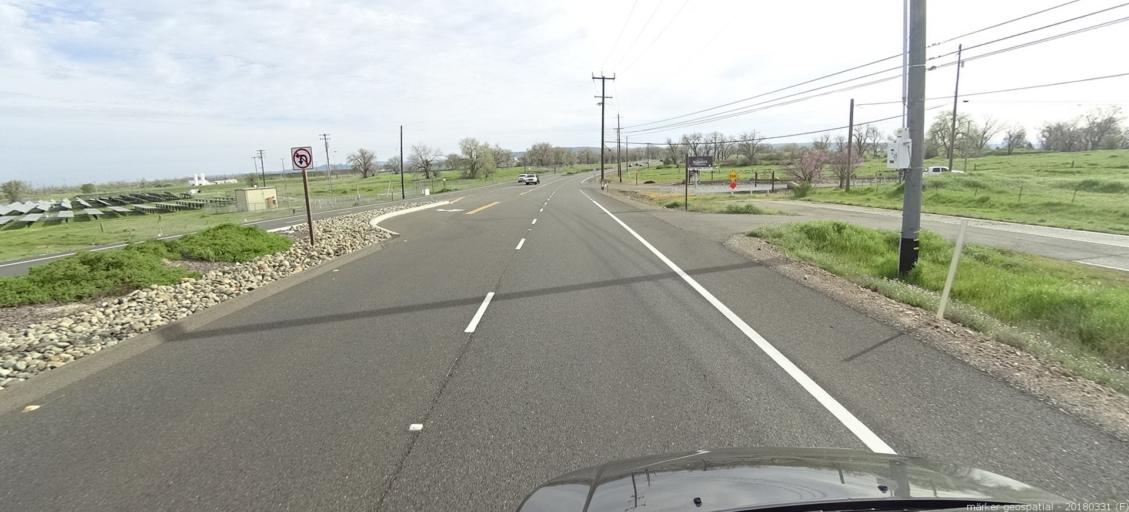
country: US
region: California
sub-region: Sacramento County
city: Folsom
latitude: 38.6075
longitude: -121.1683
